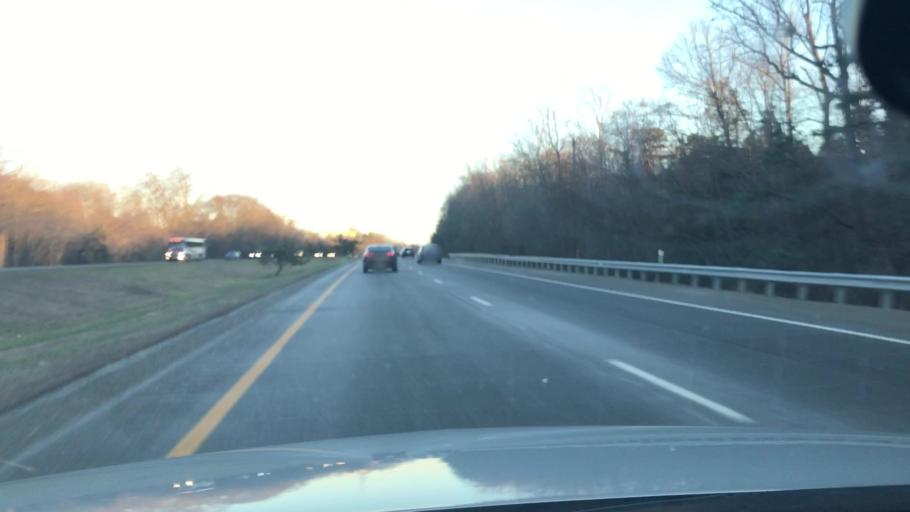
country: US
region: New Jersey
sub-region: Gloucester County
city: Turnersville
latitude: 39.7534
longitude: -75.0315
